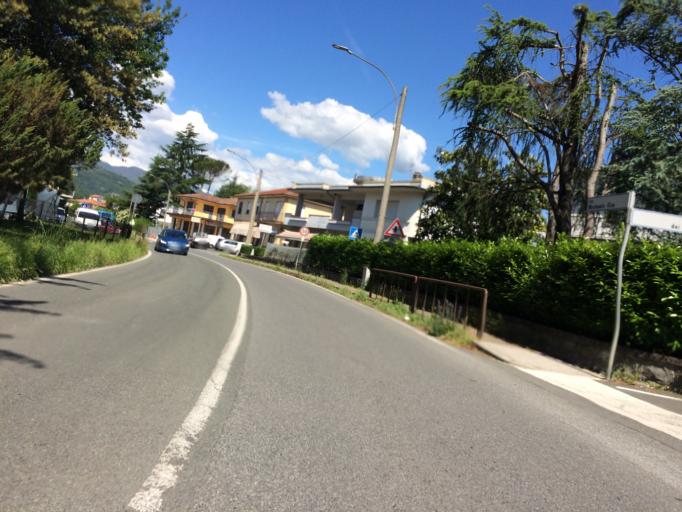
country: IT
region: Tuscany
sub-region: Provincia di Massa-Carrara
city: Terrarossa
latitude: 44.2305
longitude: 9.9644
